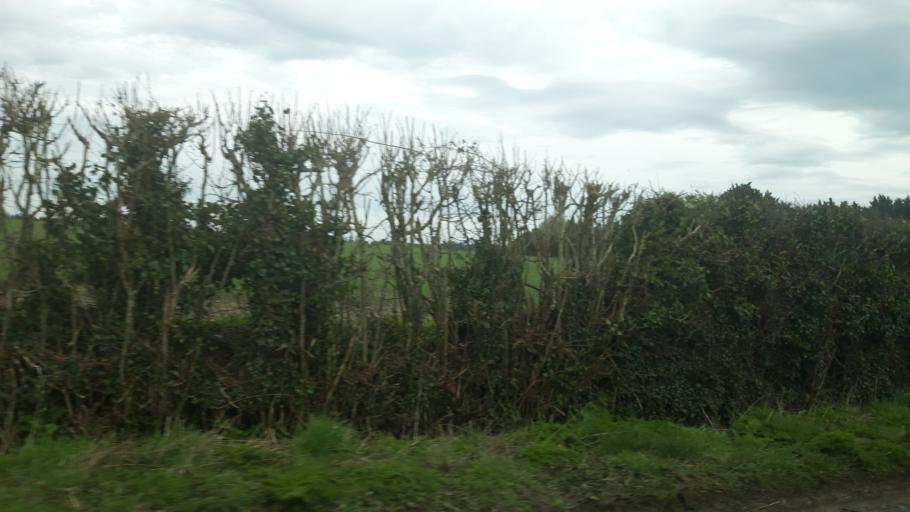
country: IE
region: Leinster
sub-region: Kildare
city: Clane
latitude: 53.3061
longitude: -6.7140
